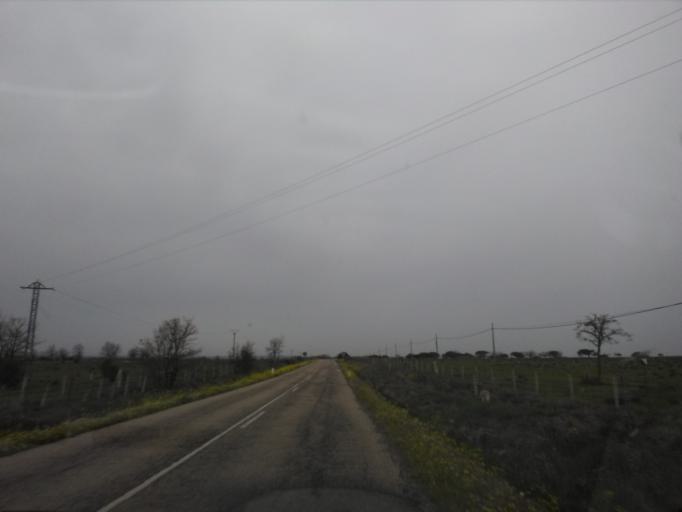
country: ES
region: Castille and Leon
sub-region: Provincia de Salamanca
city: Vitigudino
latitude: 40.9943
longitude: -6.4492
